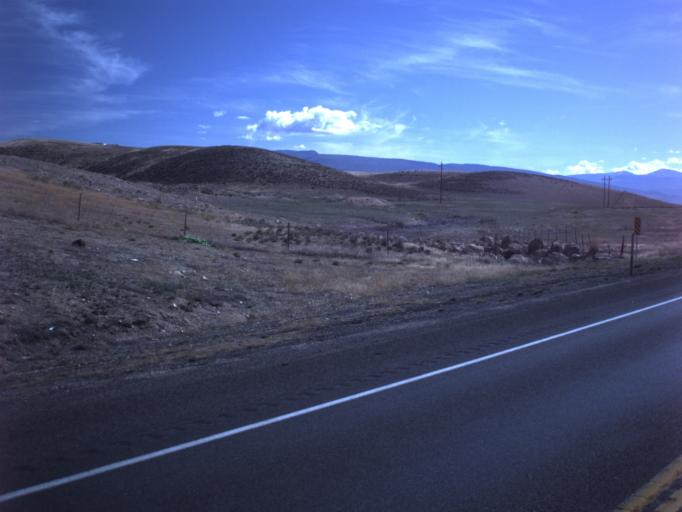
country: US
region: Utah
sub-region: Sanpete County
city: Gunnison
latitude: 39.1737
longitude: -111.8355
